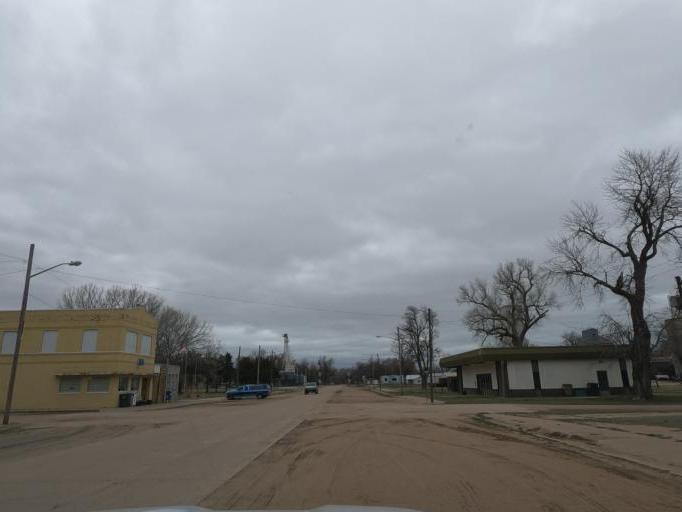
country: US
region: Kansas
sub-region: Stafford County
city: Stafford
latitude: 37.9588
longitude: -98.4085
